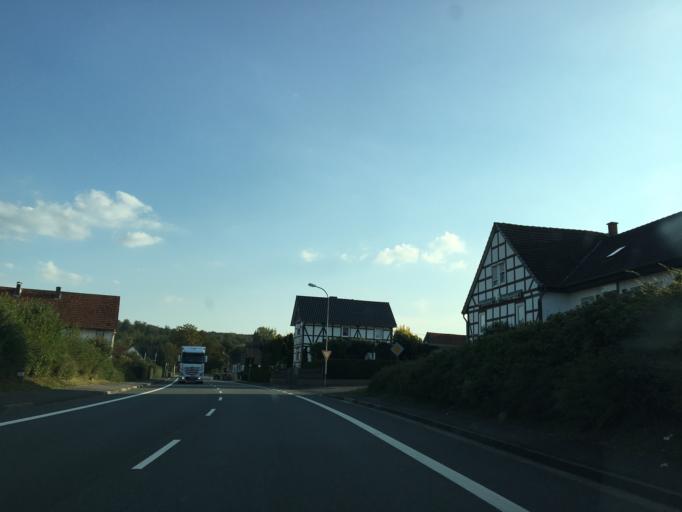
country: DE
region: Hesse
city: Frankenberg
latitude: 51.0214
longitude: 8.8047
